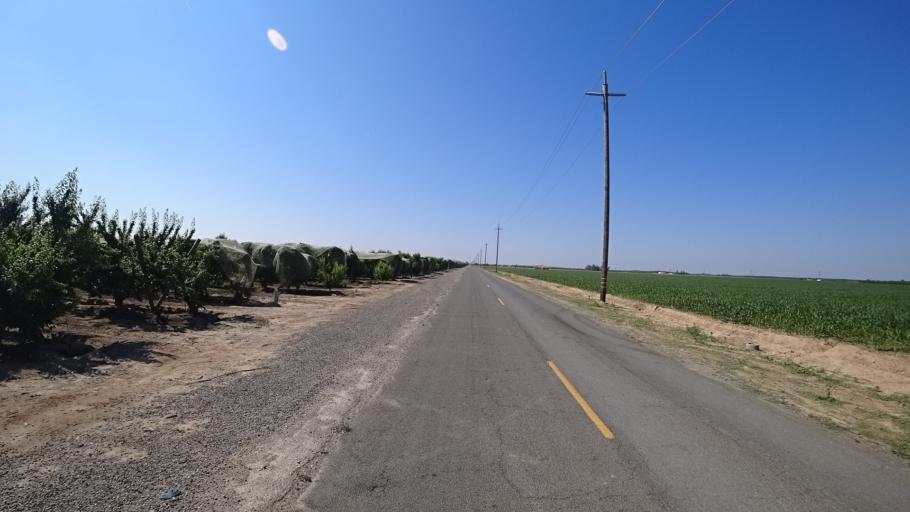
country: US
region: California
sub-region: Kings County
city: Lucerne
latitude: 36.3993
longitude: -119.5829
